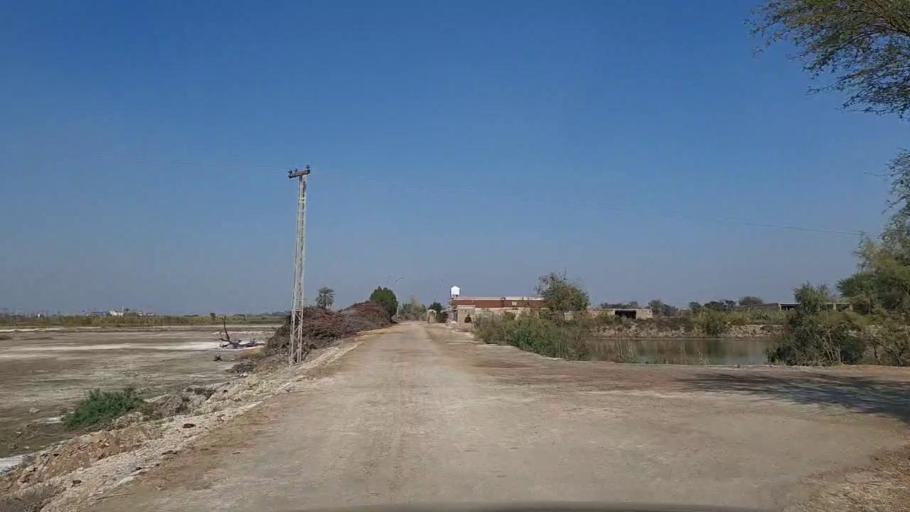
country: PK
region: Sindh
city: Bandhi
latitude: 26.5240
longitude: 68.3109
